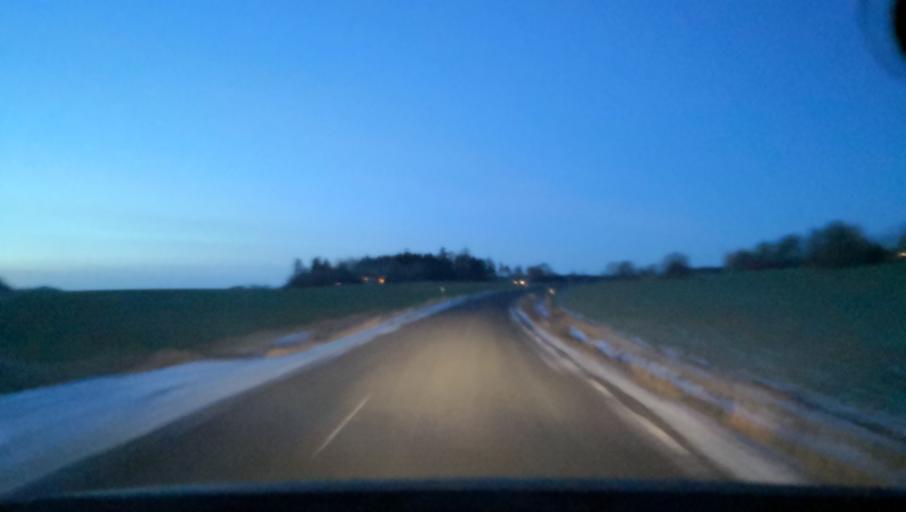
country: SE
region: Soedermanland
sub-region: Katrineholms Kommun
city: Katrineholm
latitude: 59.0783
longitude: 16.3423
